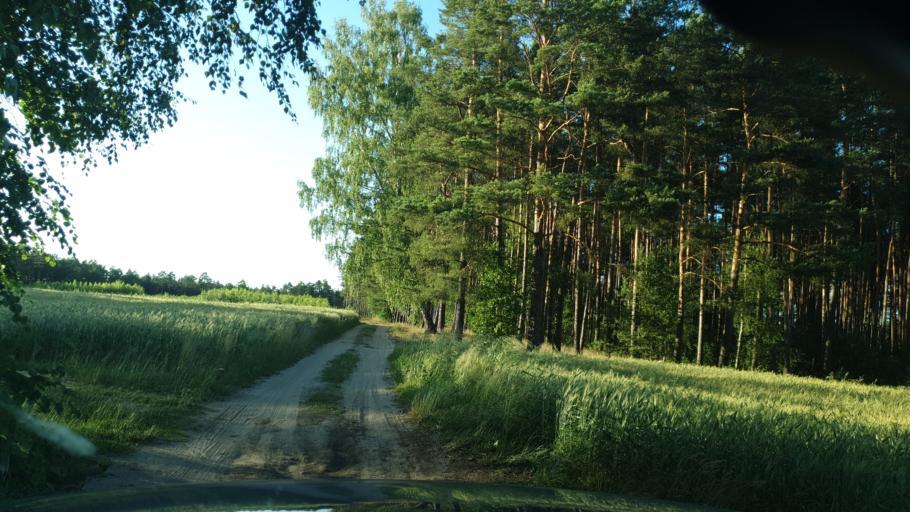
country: PL
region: Pomeranian Voivodeship
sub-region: Powiat bytowski
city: Lipnica
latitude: 53.8817
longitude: 17.4268
